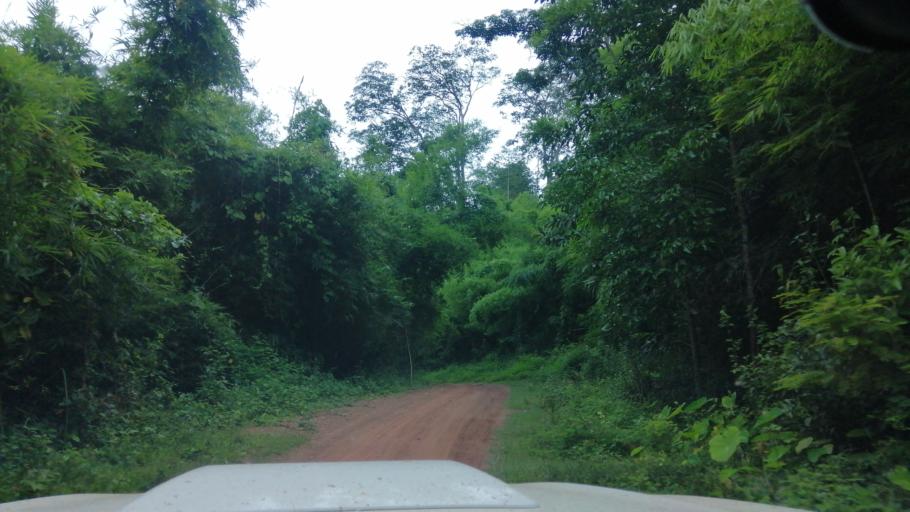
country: TH
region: Nan
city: Mae Charim
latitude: 18.7655
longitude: 101.3055
